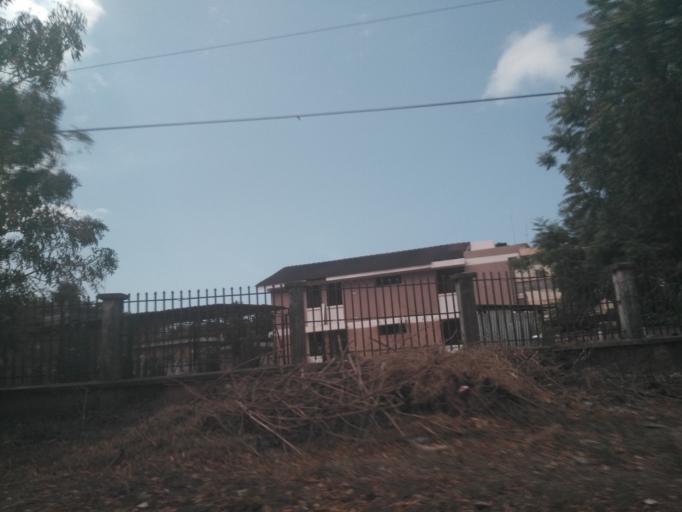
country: TZ
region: Dar es Salaam
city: Magomeni
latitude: -6.7489
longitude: 39.2763
